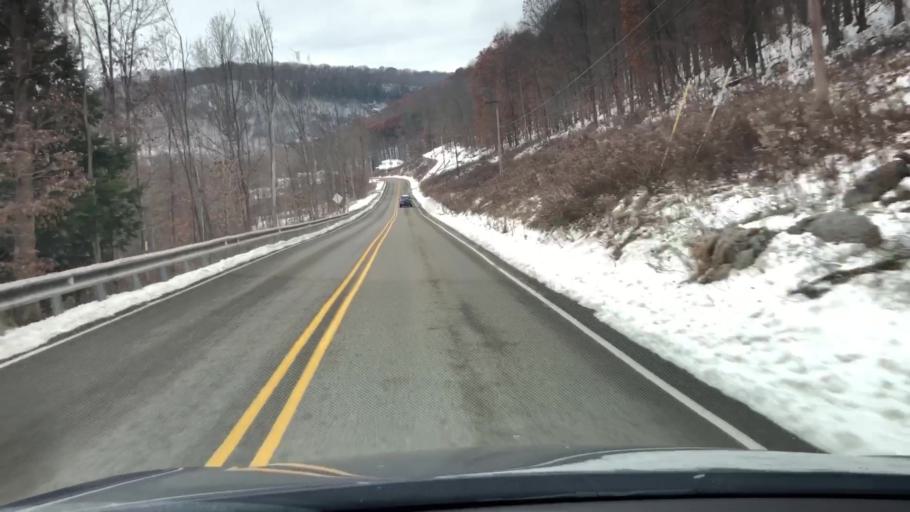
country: US
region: Pennsylvania
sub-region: Elk County
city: Saint Marys
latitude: 41.2774
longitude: -78.4670
